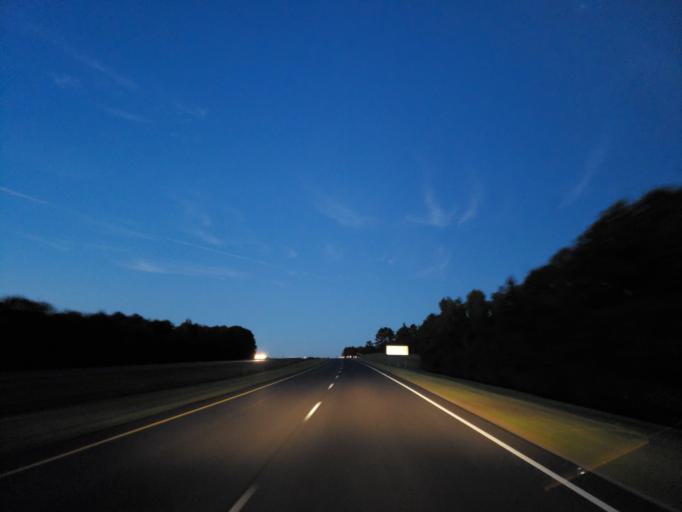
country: US
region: Mississippi
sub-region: Clarke County
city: Quitman
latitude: 32.0037
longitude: -88.6920
